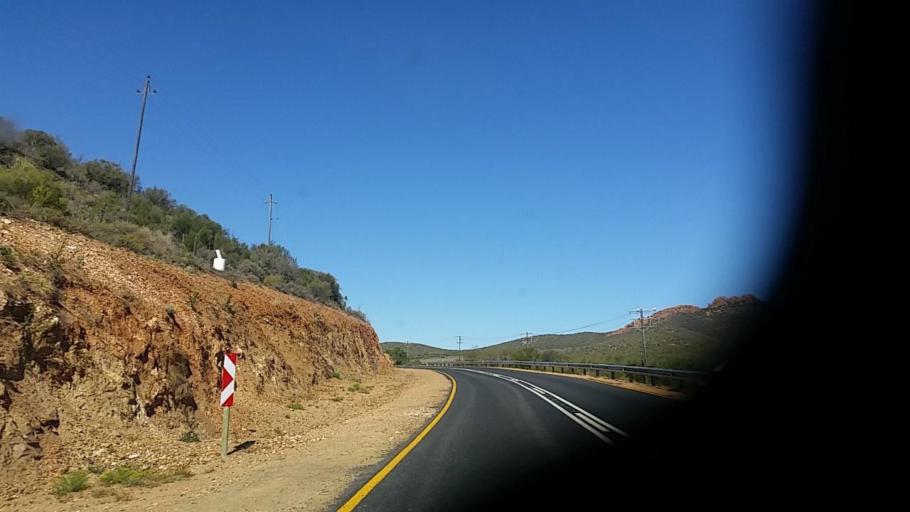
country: ZA
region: Western Cape
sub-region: Eden District Municipality
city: Oudtshoorn
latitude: -33.4872
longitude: 22.5955
